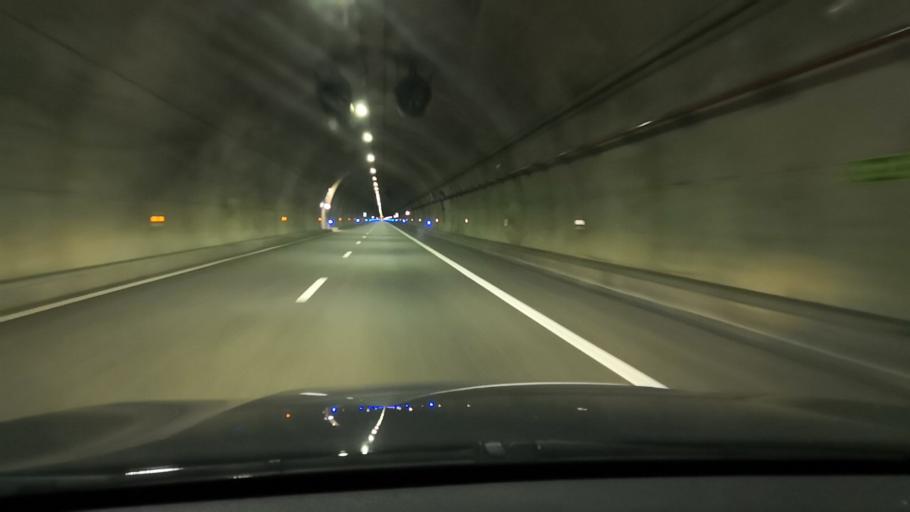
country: PT
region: Vila Real
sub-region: Mesao Frio
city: Mesao Frio
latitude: 41.2731
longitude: -7.9045
